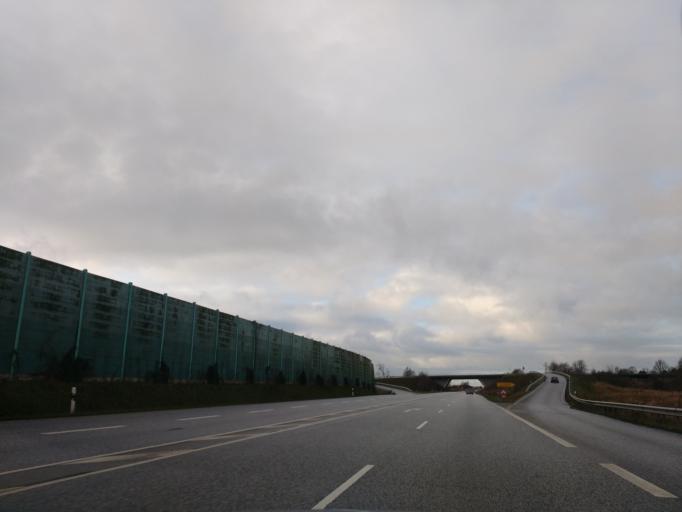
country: DE
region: Schleswig-Holstein
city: Heiligenstedten
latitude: 53.9351
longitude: 9.4743
